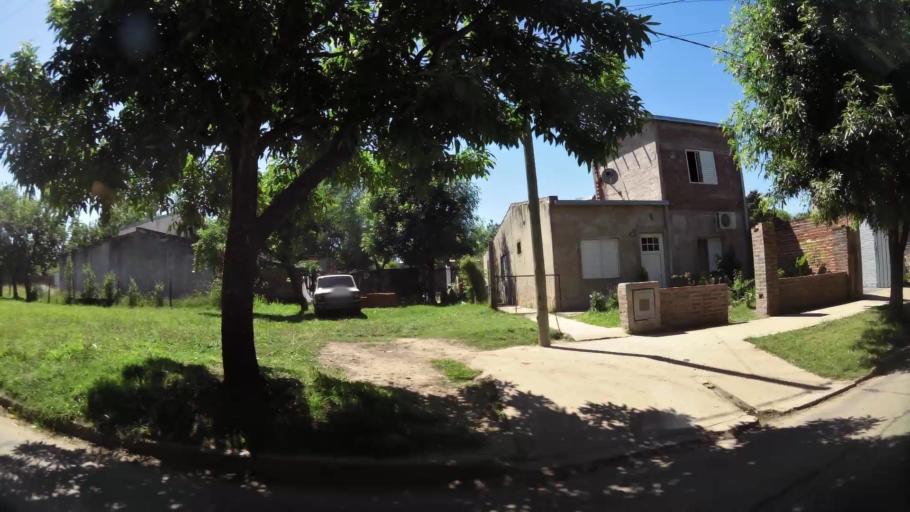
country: AR
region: Santa Fe
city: Esperanza
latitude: -31.4381
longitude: -60.9348
